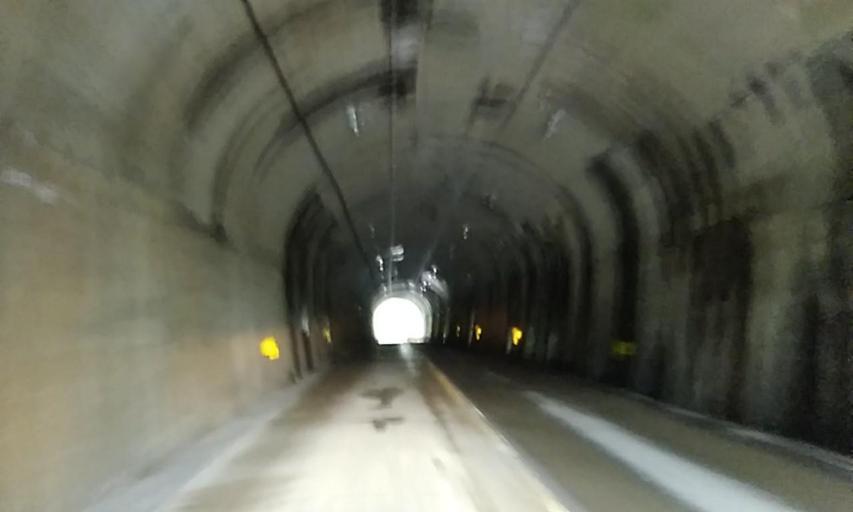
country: JP
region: Mie
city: Ise
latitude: 34.2925
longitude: 136.5312
